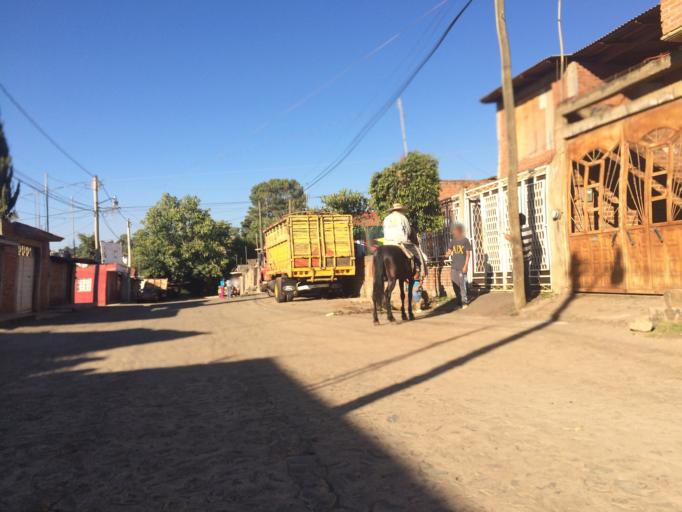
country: MX
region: Michoacan
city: Patzcuaro
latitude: 19.5056
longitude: -101.5978
